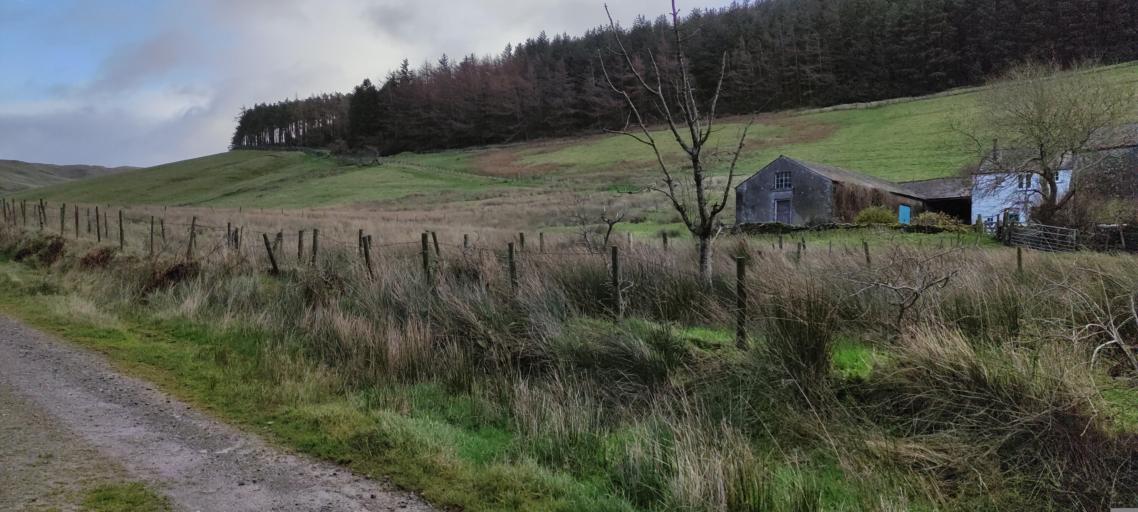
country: GB
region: England
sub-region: Cumbria
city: Cockermouth
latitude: 54.6212
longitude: -3.2669
